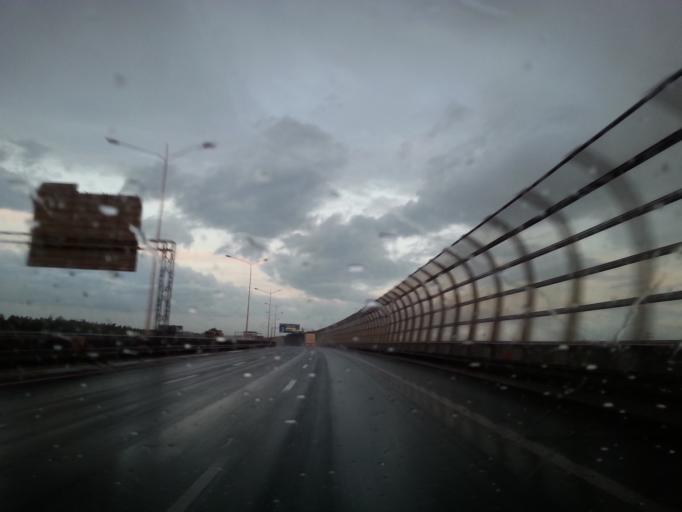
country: PL
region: Lower Silesian Voivodeship
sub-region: Powiat wroclawski
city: Smolec
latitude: 51.1234
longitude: 16.9318
